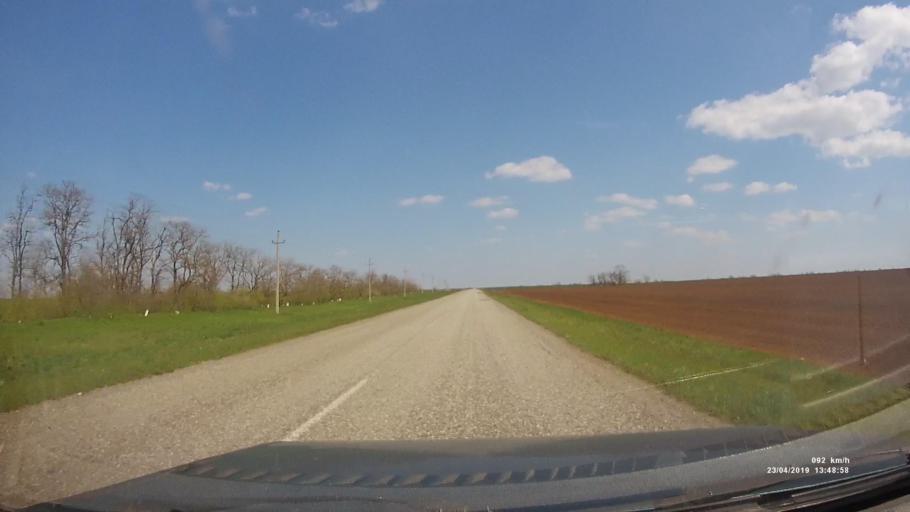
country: RU
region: Kalmykiya
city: Yashalta
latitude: 46.5992
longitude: 42.8843
